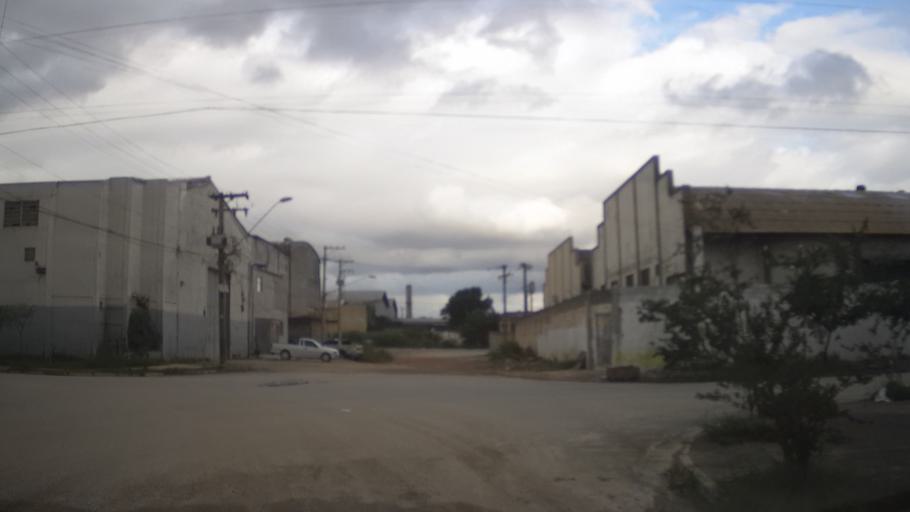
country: BR
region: Sao Paulo
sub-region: Guarulhos
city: Guarulhos
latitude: -23.4655
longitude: -46.4793
